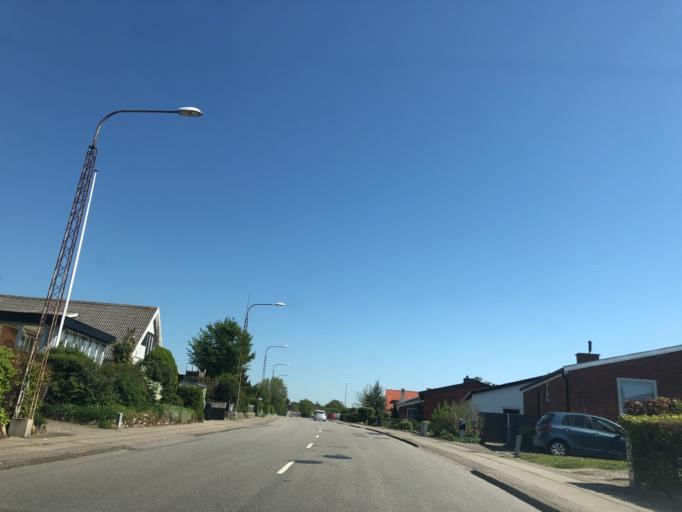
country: DK
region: Zealand
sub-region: Slagelse Kommune
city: Korsor
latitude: 55.3227
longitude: 11.1512
